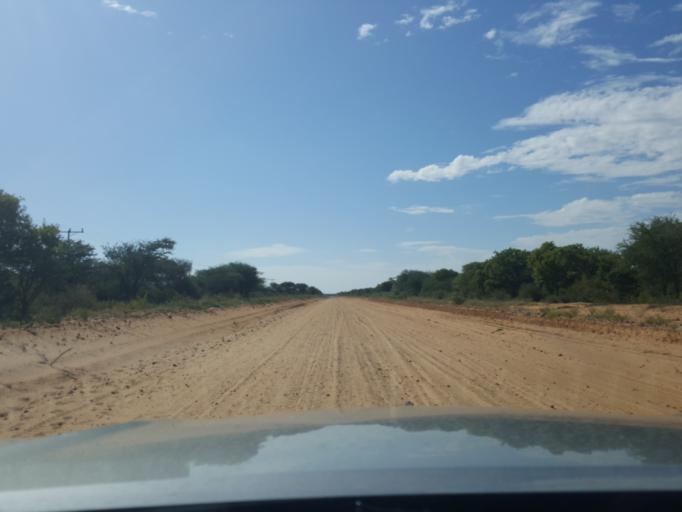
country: BW
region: Kweneng
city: Khudumelapye
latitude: -23.7166
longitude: 24.7338
